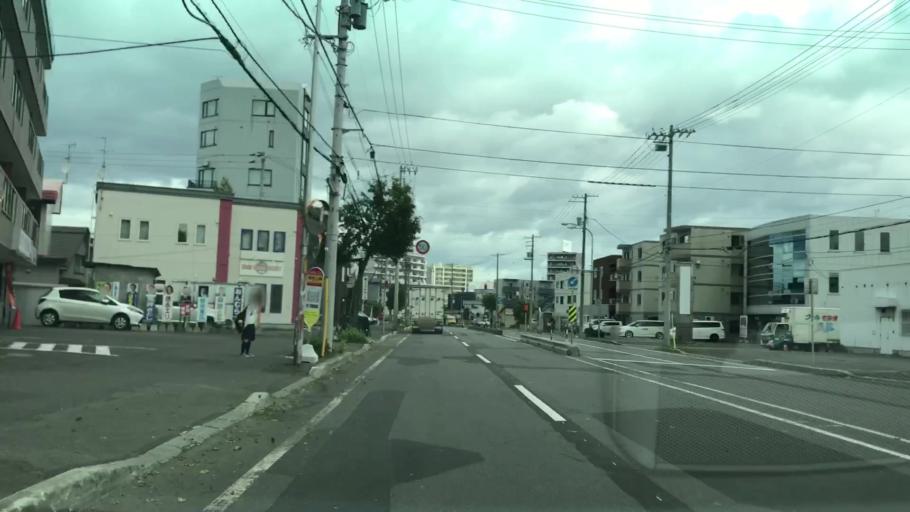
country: JP
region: Hokkaido
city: Sapporo
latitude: 42.9936
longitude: 141.4410
